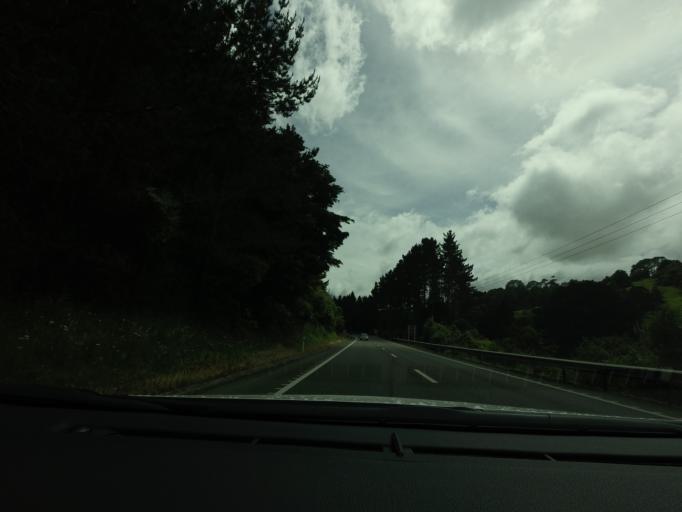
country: NZ
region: Auckland
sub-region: Auckland
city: Warkworth
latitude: -36.5093
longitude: 174.6712
